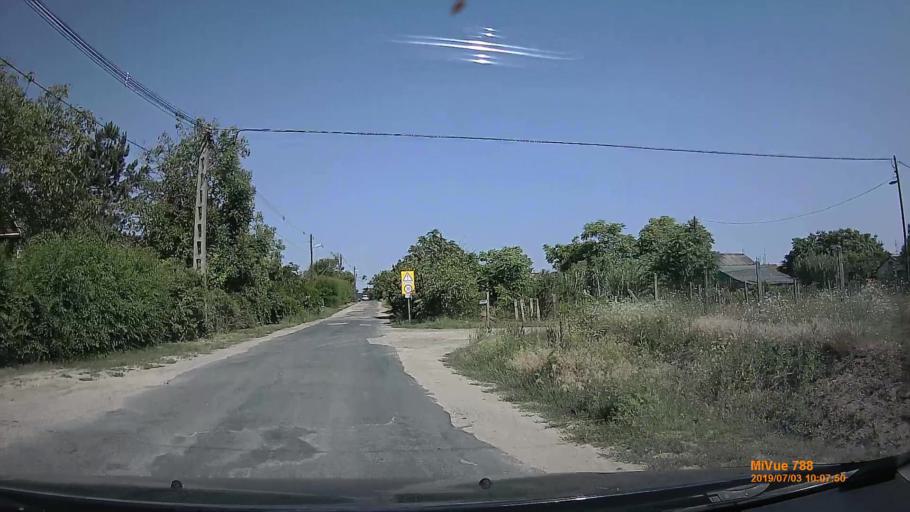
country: HU
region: Gyor-Moson-Sopron
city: Gyor
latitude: 47.7180
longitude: 17.7156
